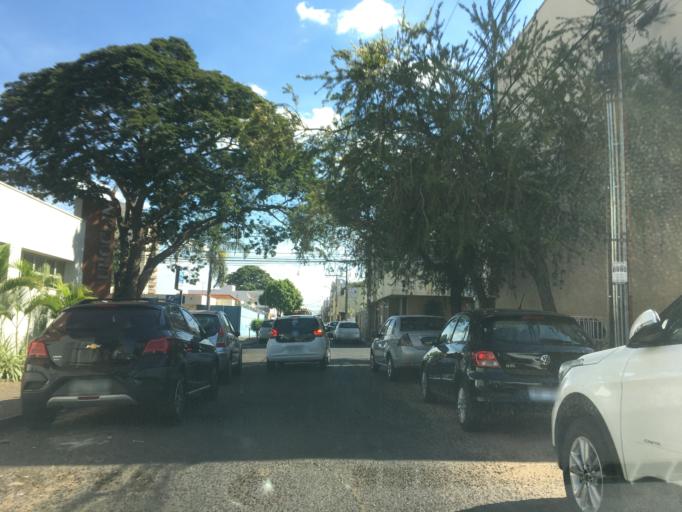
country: BR
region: Minas Gerais
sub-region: Uberlandia
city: Uberlandia
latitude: -18.9152
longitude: -48.2843
